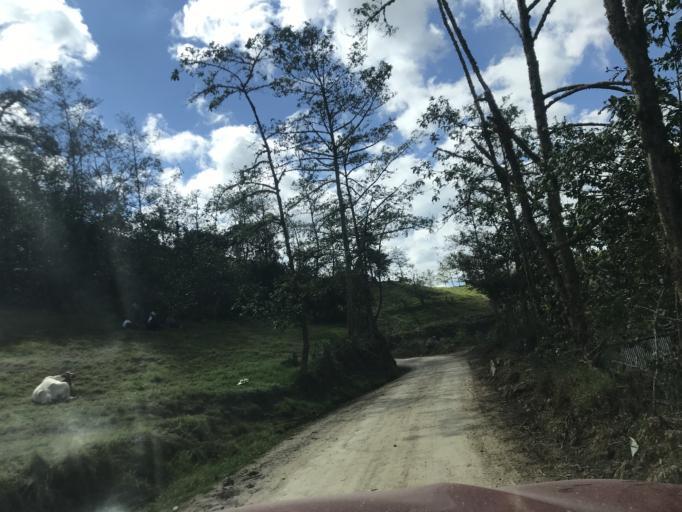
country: PE
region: Cajamarca
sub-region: Provincia de Chota
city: Querocoto
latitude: -6.3448
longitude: -79.0477
